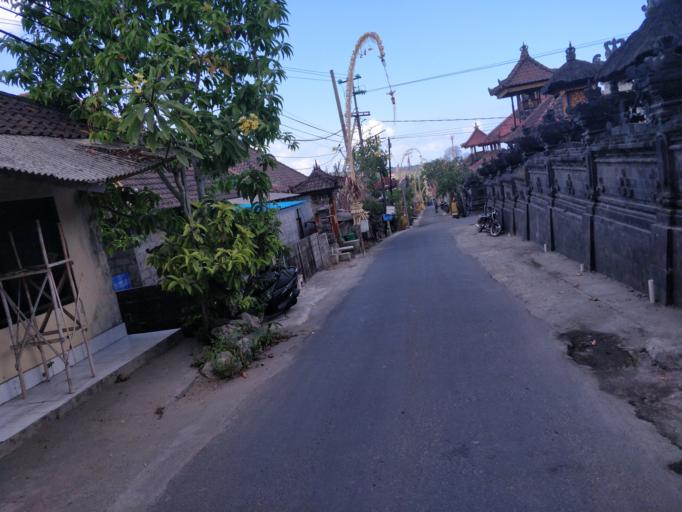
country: ID
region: Bali
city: Lembongan Kawan
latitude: -8.6890
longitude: 115.4412
